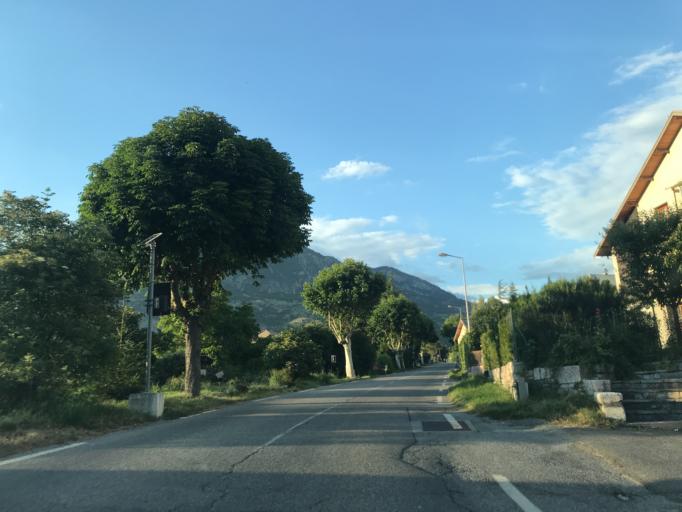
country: FR
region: Provence-Alpes-Cote d'Azur
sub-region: Departement des Hautes-Alpes
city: Guillestre
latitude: 44.6584
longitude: 6.6566
